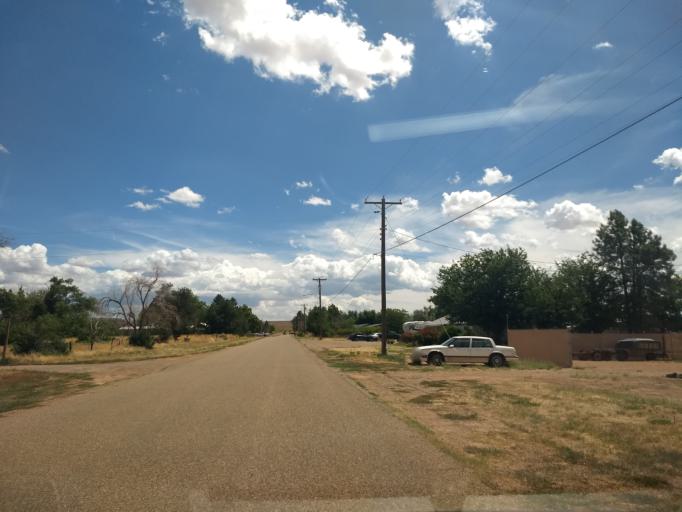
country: US
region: Arizona
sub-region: Coconino County
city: Fredonia
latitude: 36.9473
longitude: -112.5236
